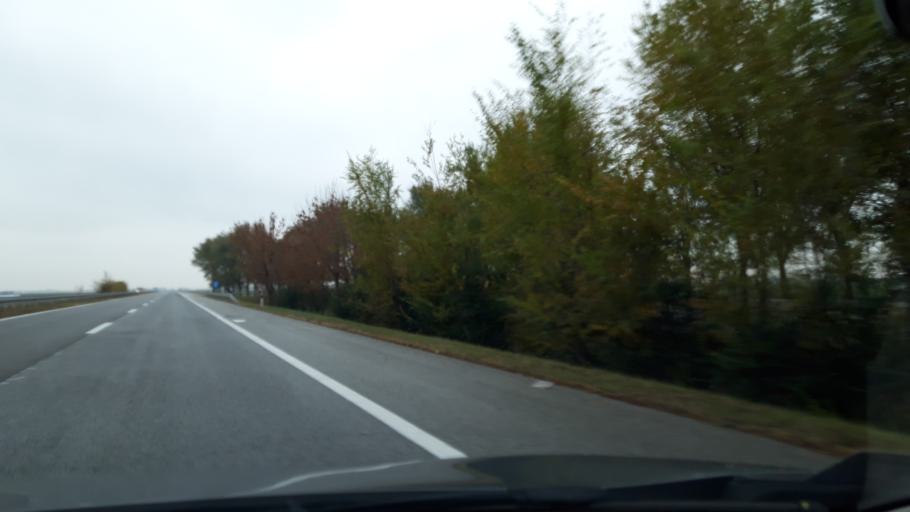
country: RS
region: Autonomna Pokrajina Vojvodina
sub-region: Severnobacki Okrug
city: Subotica
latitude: 45.9972
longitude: 19.7209
